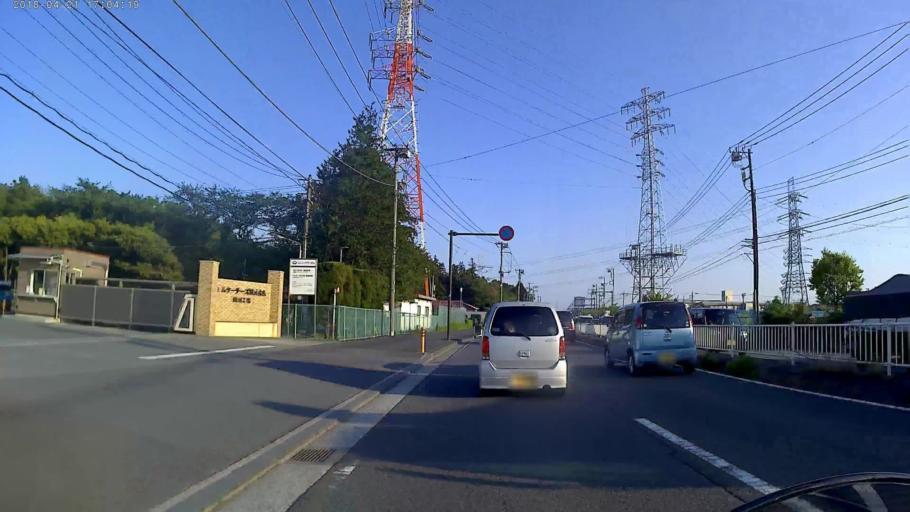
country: JP
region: Kanagawa
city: Minami-rinkan
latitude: 35.4269
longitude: 139.4328
